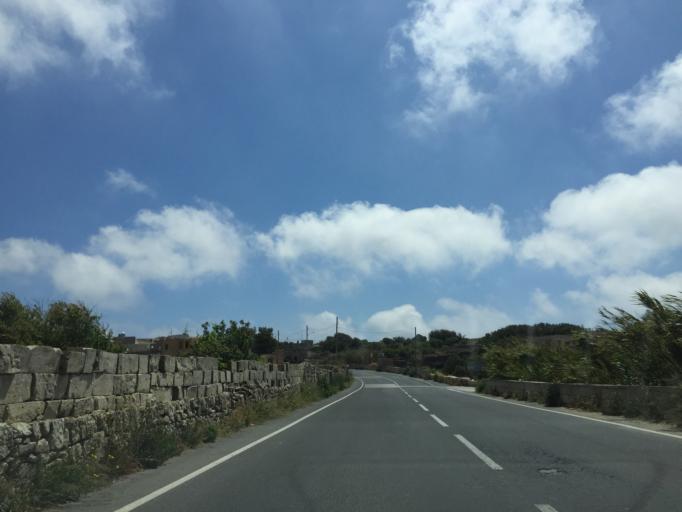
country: MT
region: Dingli
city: Dingli
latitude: 35.8671
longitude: 14.3904
